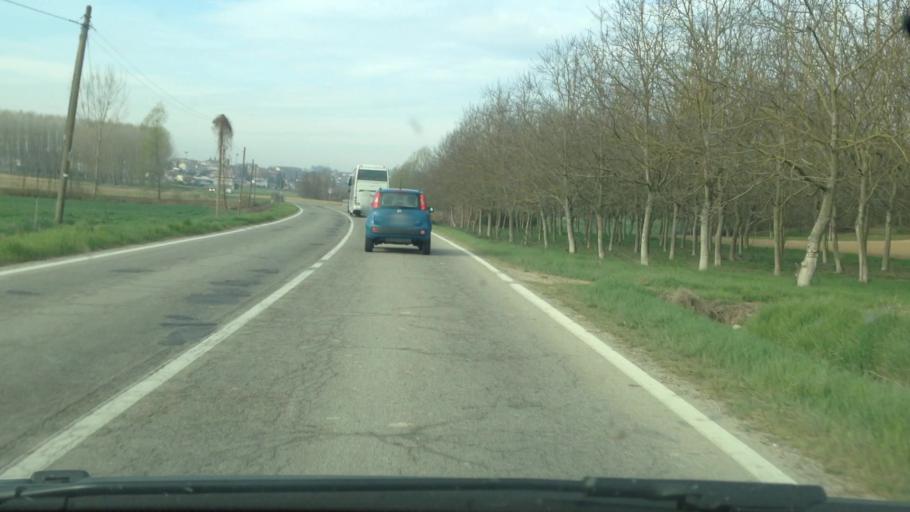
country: IT
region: Piedmont
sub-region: Provincia di Asti
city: San Damiano d'Asti
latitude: 44.8481
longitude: 8.0827
